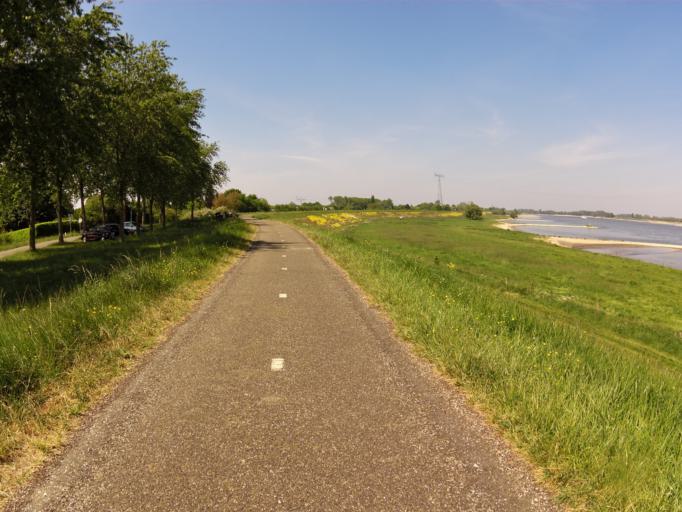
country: NL
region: Gelderland
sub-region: Gemeente Maasdriel
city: Heerewaarden
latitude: 51.8039
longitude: 5.3379
